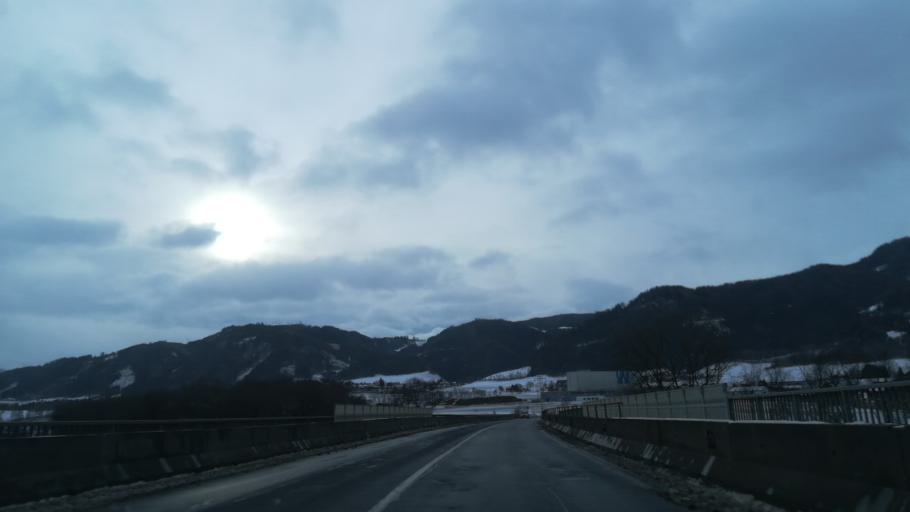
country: AT
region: Styria
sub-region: Politischer Bezirk Murtal
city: Sankt Peter ob Judenburg
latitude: 47.1911
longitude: 14.5998
